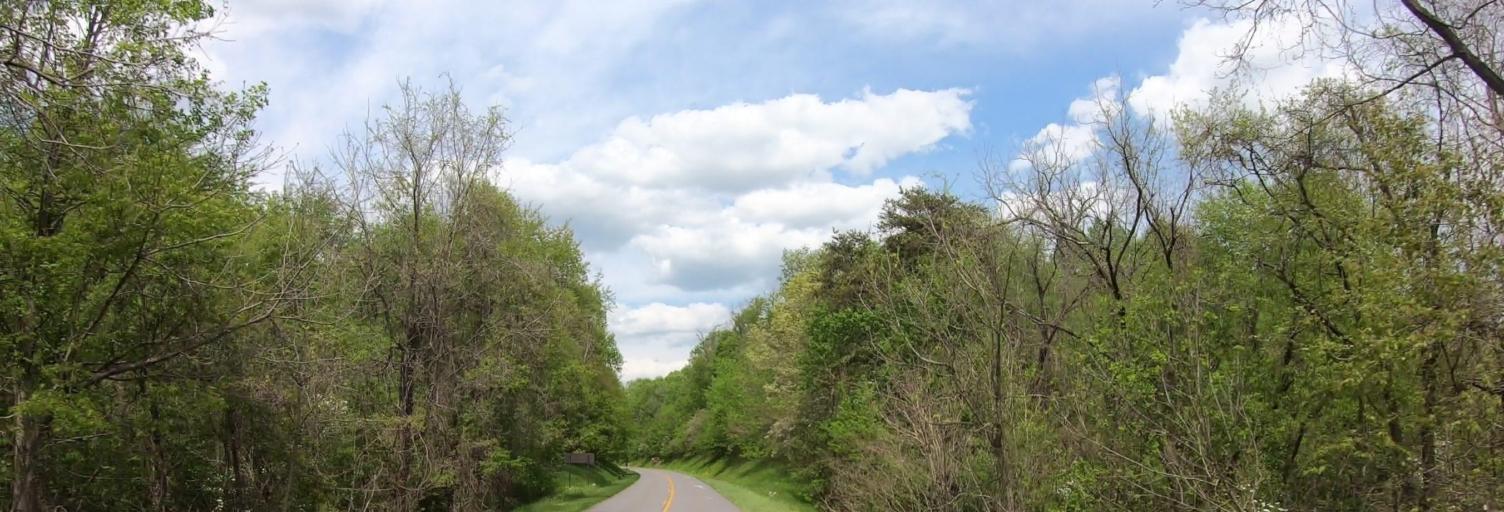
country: US
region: Virginia
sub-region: Botetourt County
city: Laymantown
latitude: 37.3512
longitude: -79.8370
